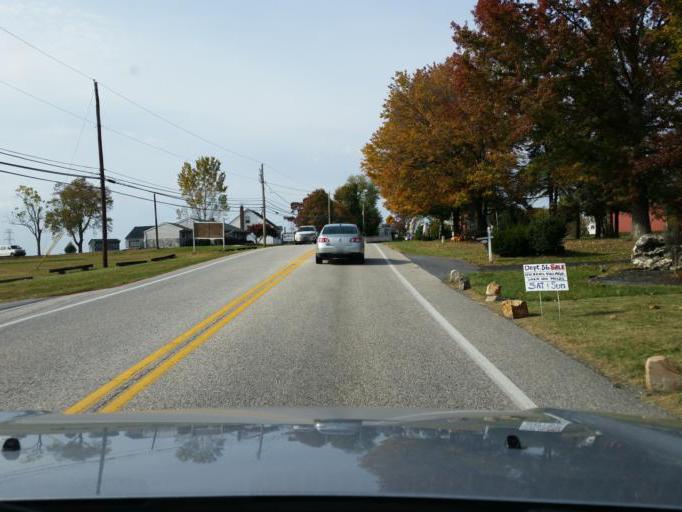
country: US
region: Pennsylvania
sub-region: Dauphin County
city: Skyline View
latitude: 40.3224
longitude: -76.7085
